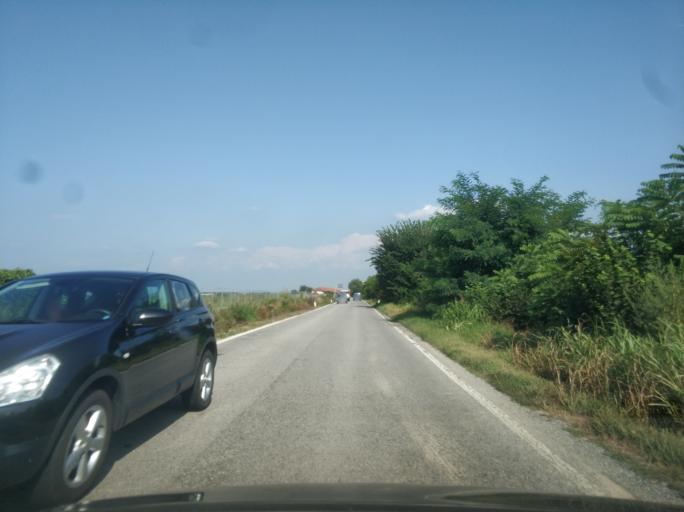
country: IT
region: Piedmont
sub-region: Provincia di Cuneo
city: Centallo
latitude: 44.5363
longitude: 7.6131
